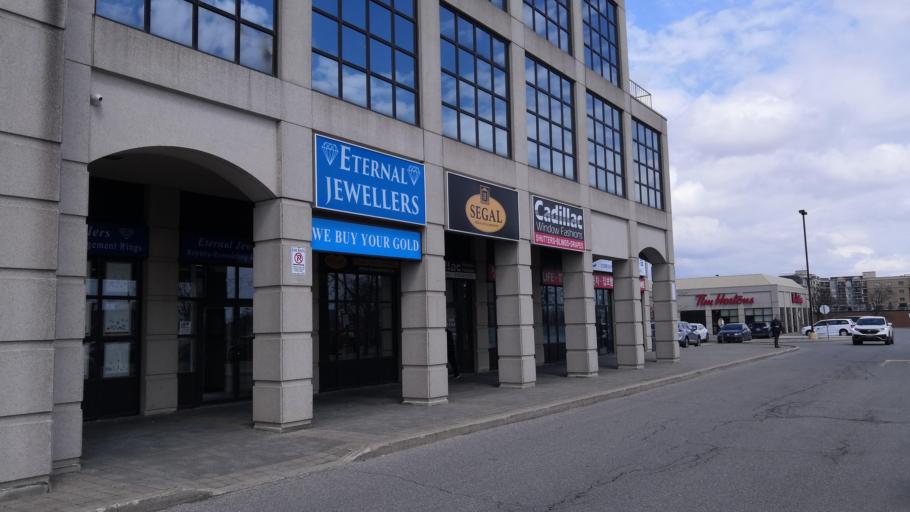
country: CA
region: Ontario
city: Concord
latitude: 43.7869
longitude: -79.4737
